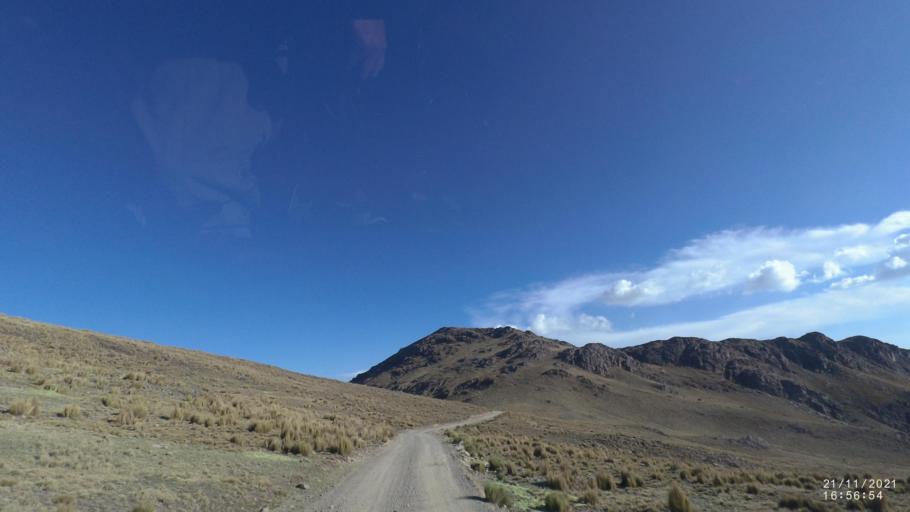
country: BO
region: Cochabamba
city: Cochabamba
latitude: -17.0951
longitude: -66.2540
